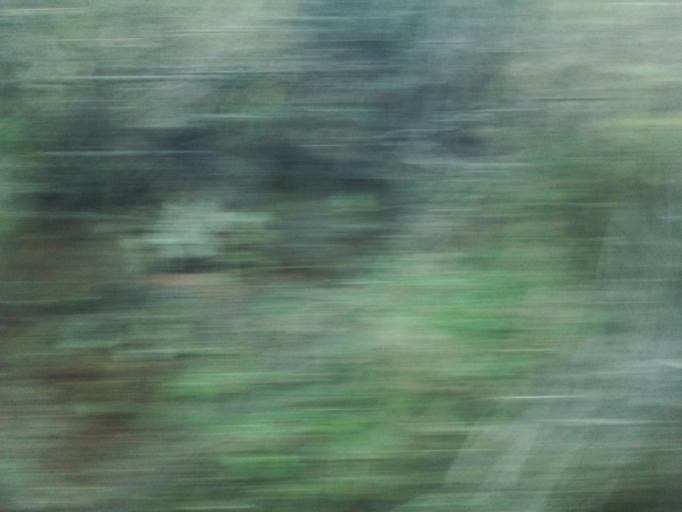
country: BR
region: Minas Gerais
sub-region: Rio Piracicaba
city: Rio Piracicaba
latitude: -19.8790
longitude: -43.1260
